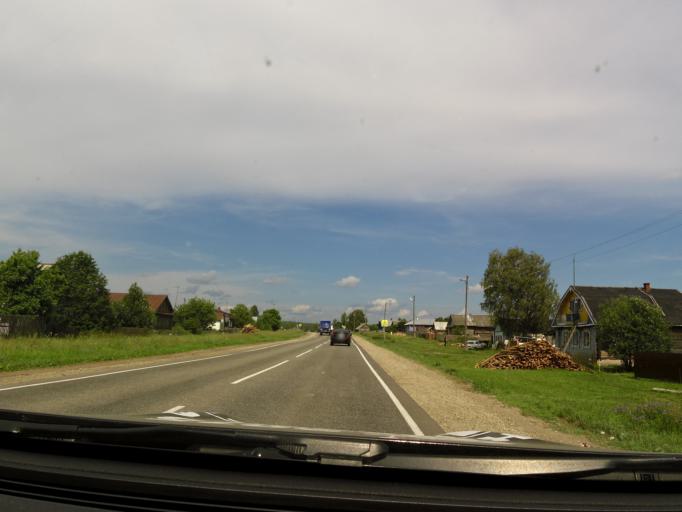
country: RU
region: Kirov
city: Vakhrushi
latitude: 58.6694
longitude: 49.9388
